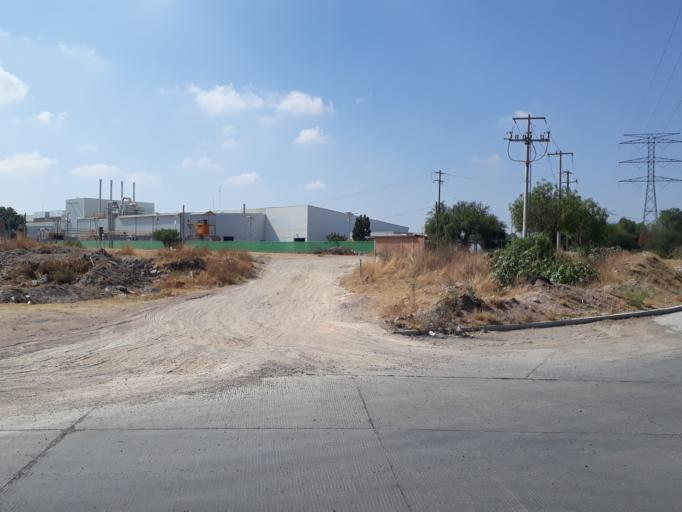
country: MX
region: Aguascalientes
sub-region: Aguascalientes
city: San Sebastian [Fraccionamiento]
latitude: 21.8071
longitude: -102.2912
